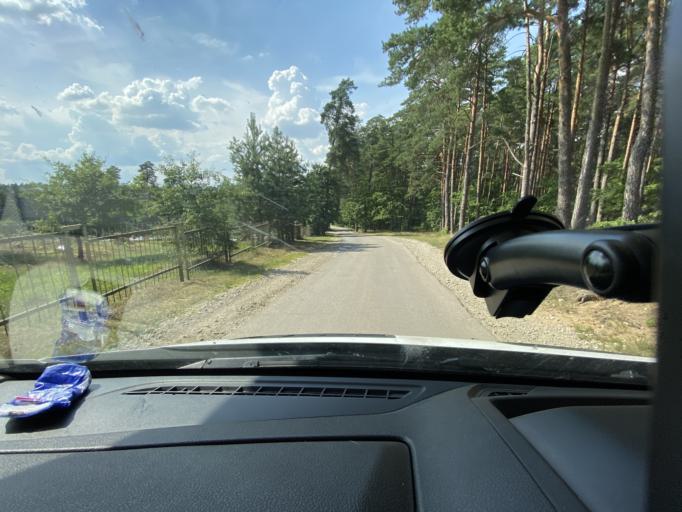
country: LT
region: Kauno apskritis
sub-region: Kauno rajonas
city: Karmelava
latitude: 54.9749
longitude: 24.0432
